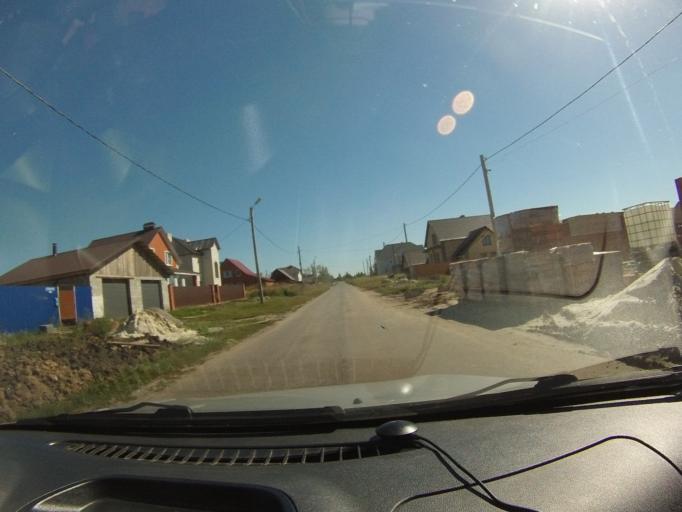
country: RU
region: Tambov
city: Komsomolets
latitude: 52.7714
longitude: 41.3595
